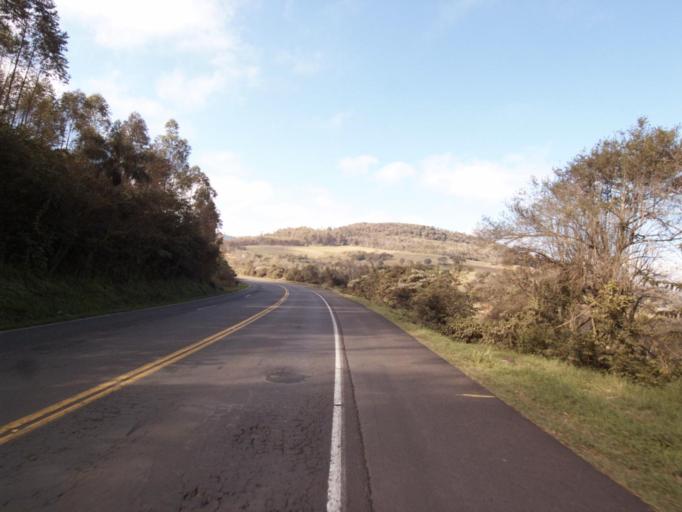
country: BR
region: Rio Grande do Sul
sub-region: Frederico Westphalen
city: Frederico Westphalen
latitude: -27.0764
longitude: -53.2310
